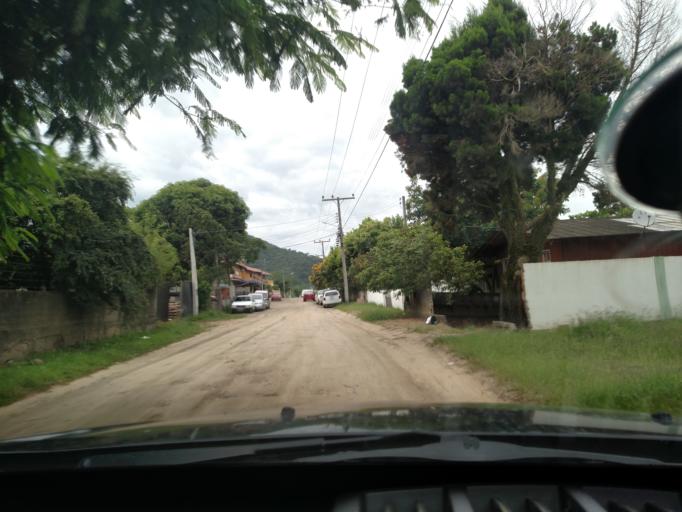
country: BR
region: Santa Catarina
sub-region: Porto Belo
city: Porto Belo
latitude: -27.1522
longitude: -48.5093
